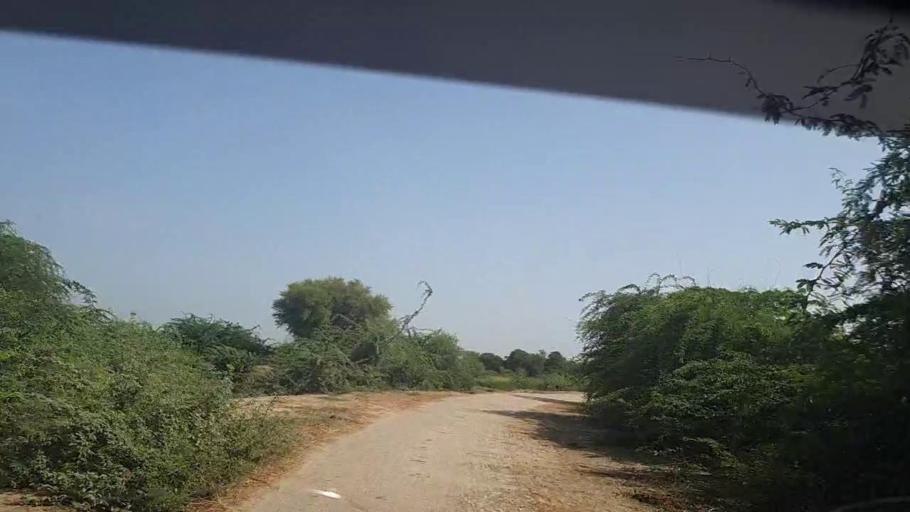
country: PK
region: Sindh
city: Rajo Khanani
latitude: 24.9633
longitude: 68.8912
